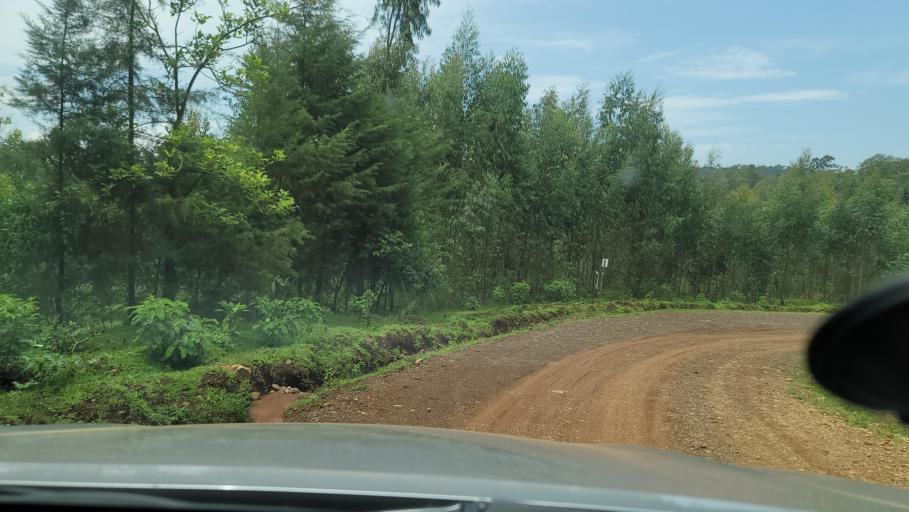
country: ET
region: Oromiya
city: Agaro
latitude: 7.7351
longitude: 36.2605
